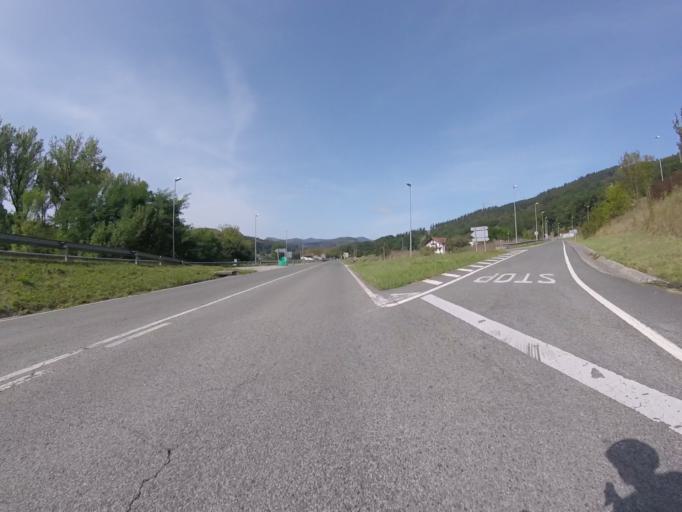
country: ES
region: Navarre
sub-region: Provincia de Navarra
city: Doneztebe
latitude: 43.1322
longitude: -1.6413
